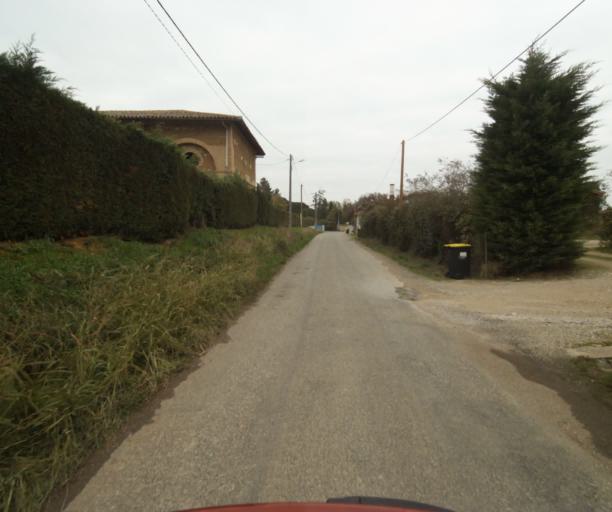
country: FR
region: Midi-Pyrenees
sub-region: Departement du Tarn-et-Garonne
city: Verdun-sur-Garonne
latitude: 43.8054
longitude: 1.2300
